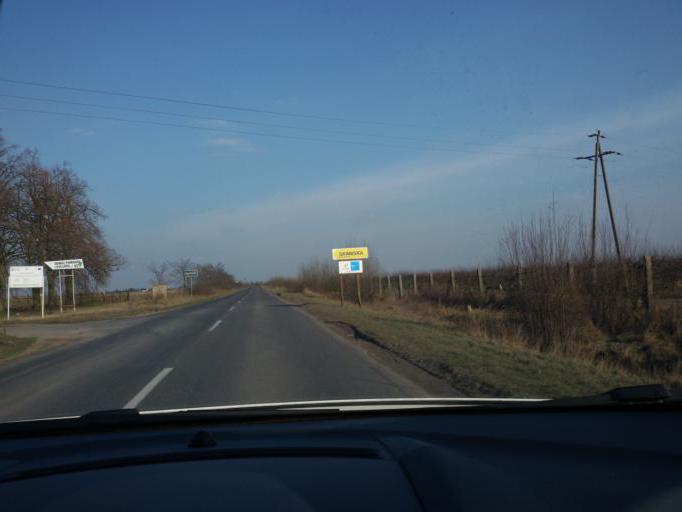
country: PL
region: Greater Poland Voivodeship
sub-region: Powiat gostynski
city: Krobia
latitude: 51.7682
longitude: 16.9442
